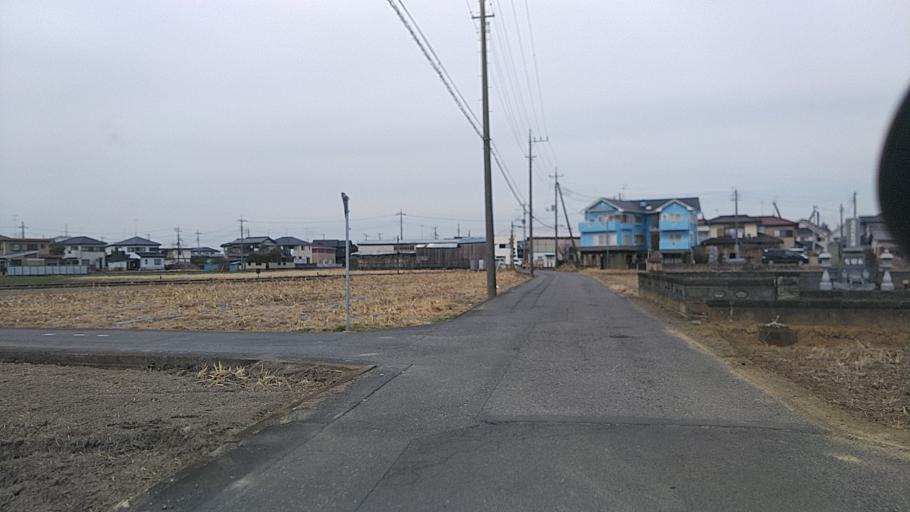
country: JP
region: Ibaraki
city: Ishige
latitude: 36.1045
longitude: 139.9748
